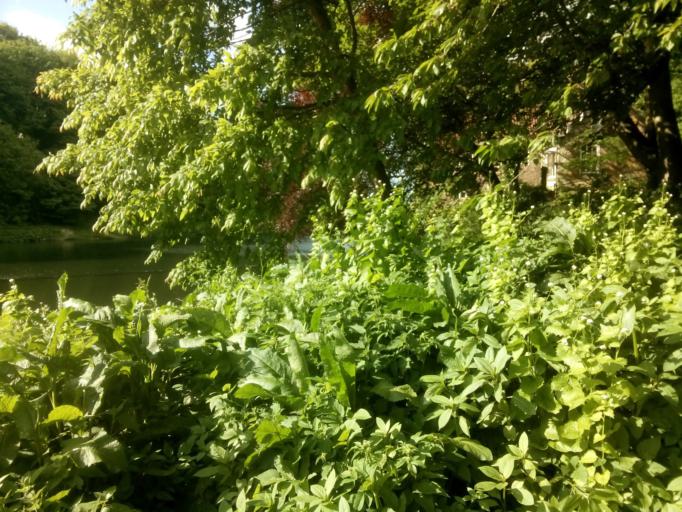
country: GB
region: England
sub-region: County Durham
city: Durham
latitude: 54.7725
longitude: -1.5787
